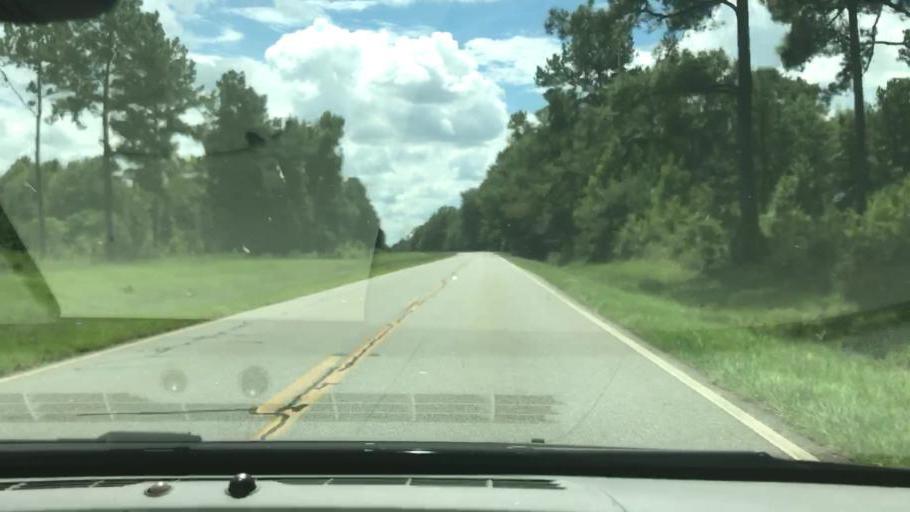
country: US
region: Georgia
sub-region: Quitman County
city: Georgetown
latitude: 32.1144
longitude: -85.0375
